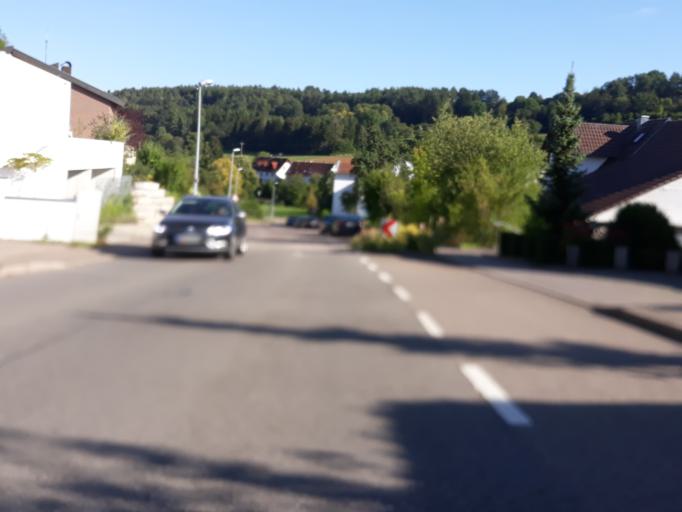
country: DE
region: Baden-Wuerttemberg
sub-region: Karlsruhe Region
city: Gechingen
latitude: 48.6799
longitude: 8.8558
